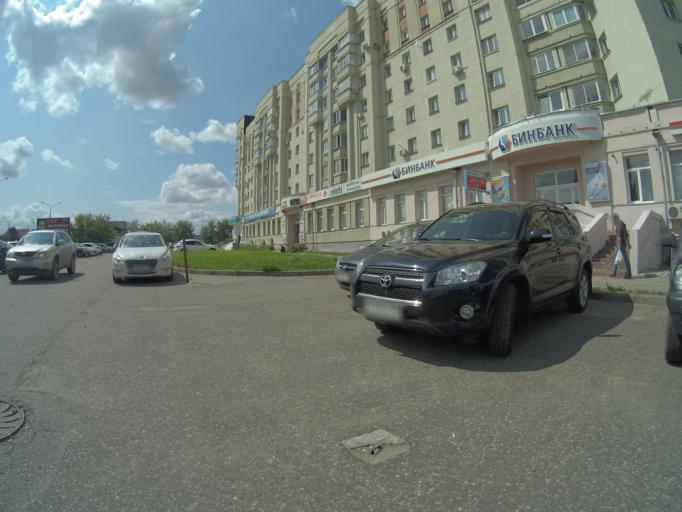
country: RU
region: Vladimir
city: Vladimir
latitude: 56.1370
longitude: 40.3935
